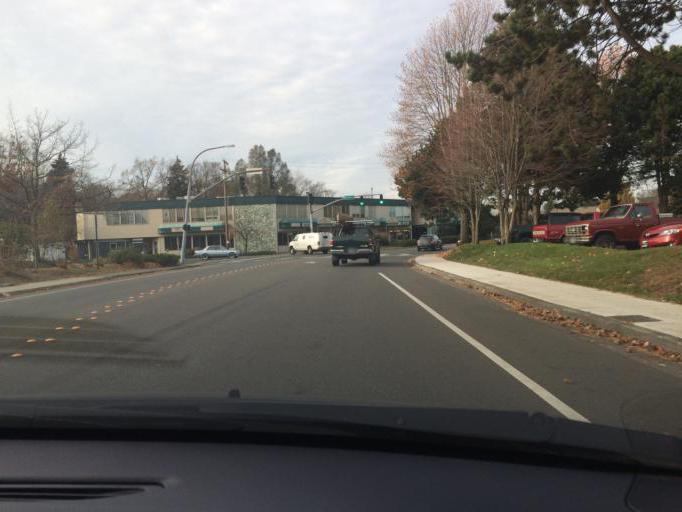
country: US
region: Washington
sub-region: Whatcom County
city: Bellingham
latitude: 48.7594
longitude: -122.4878
